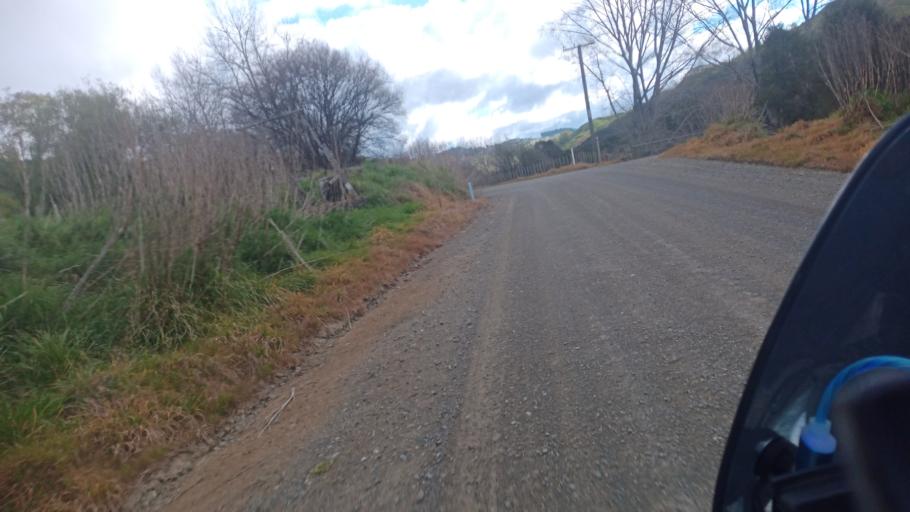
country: NZ
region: Gisborne
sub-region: Gisborne District
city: Gisborne
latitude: -38.2027
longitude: 178.2448
